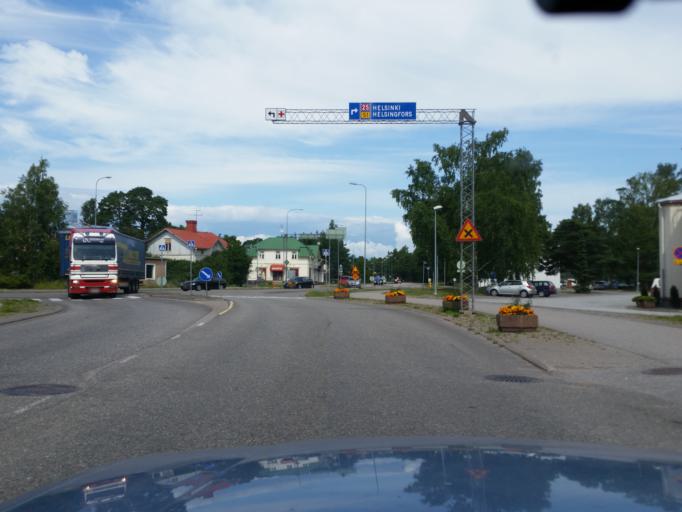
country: FI
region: Uusimaa
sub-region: Raaseporin
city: Hanko
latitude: 59.8311
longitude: 22.9899
